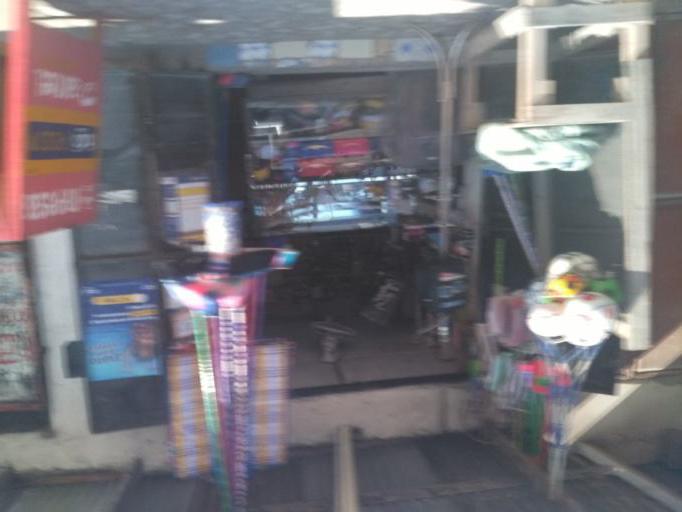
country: TZ
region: Dar es Salaam
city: Dar es Salaam
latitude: -6.8747
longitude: 39.2692
